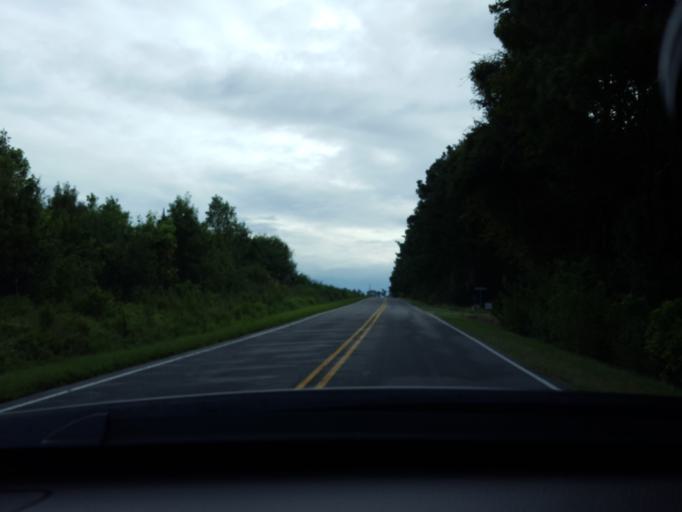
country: US
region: North Carolina
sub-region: Duplin County
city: Rose Hill
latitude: 34.9104
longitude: -78.0363
